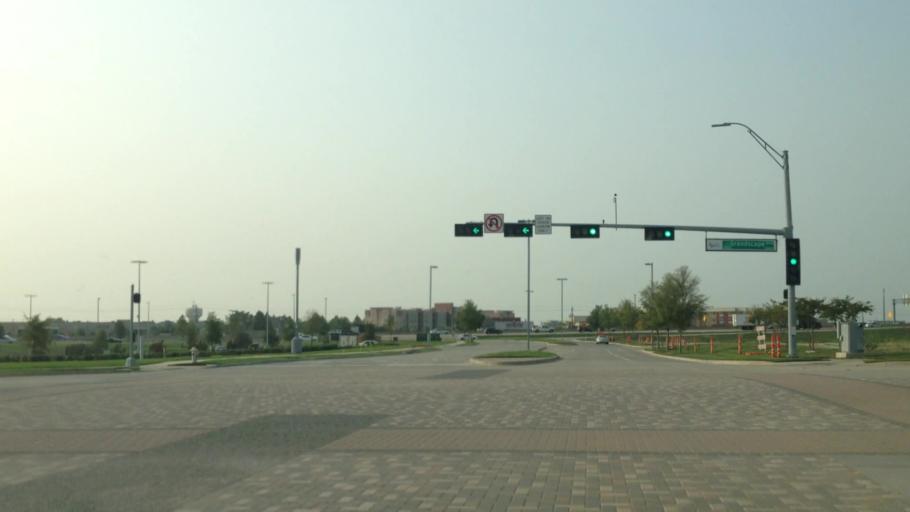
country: US
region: Texas
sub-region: Denton County
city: The Colony
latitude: 33.0777
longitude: -96.8570
